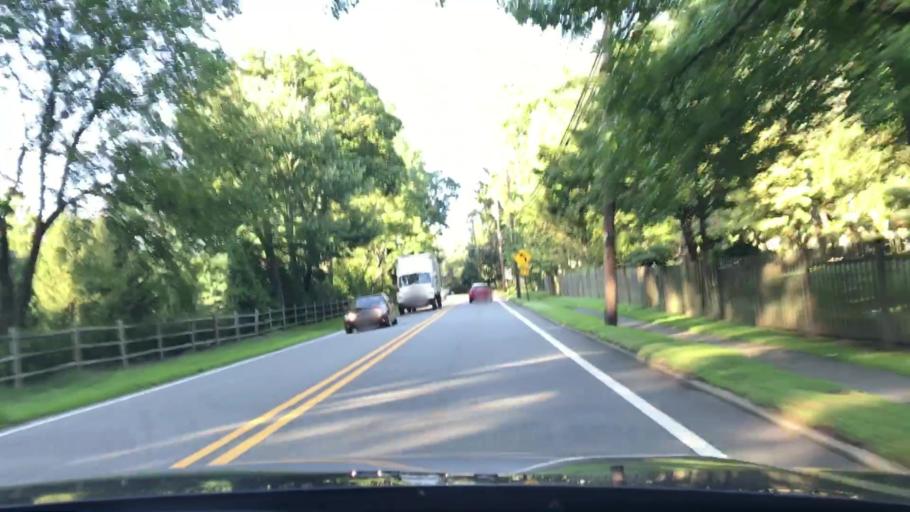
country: US
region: New Jersey
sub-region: Bergen County
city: Closter
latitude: 40.9834
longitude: -73.9395
